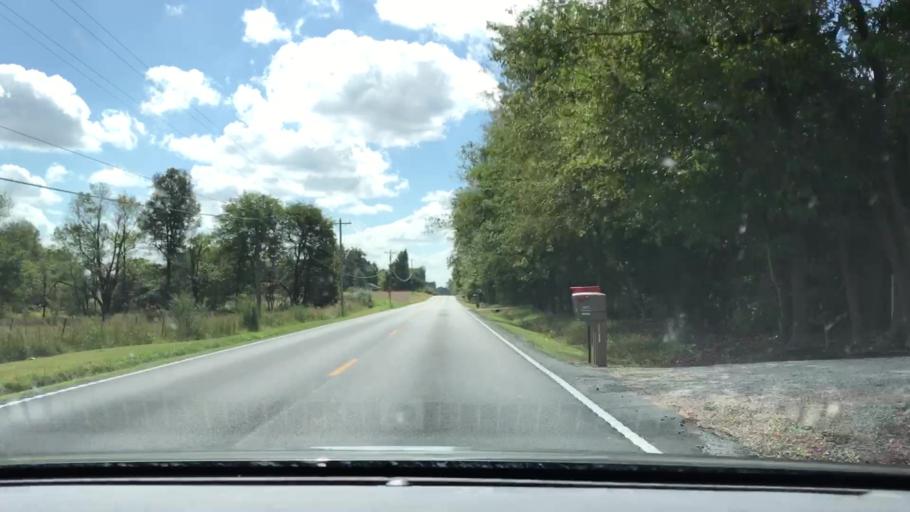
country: US
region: Kentucky
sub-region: Graves County
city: Mayfield
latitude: 36.7982
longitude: -88.5955
